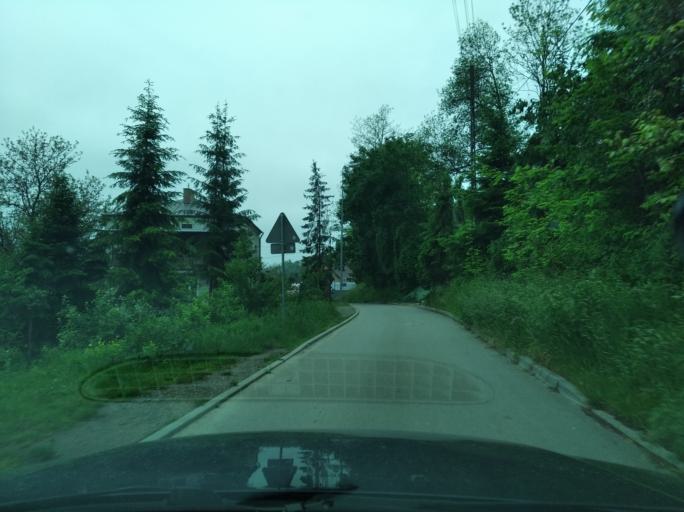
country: PL
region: Subcarpathian Voivodeship
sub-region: Powiat rzeszowski
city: Dynow
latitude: 49.8151
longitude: 22.2350
